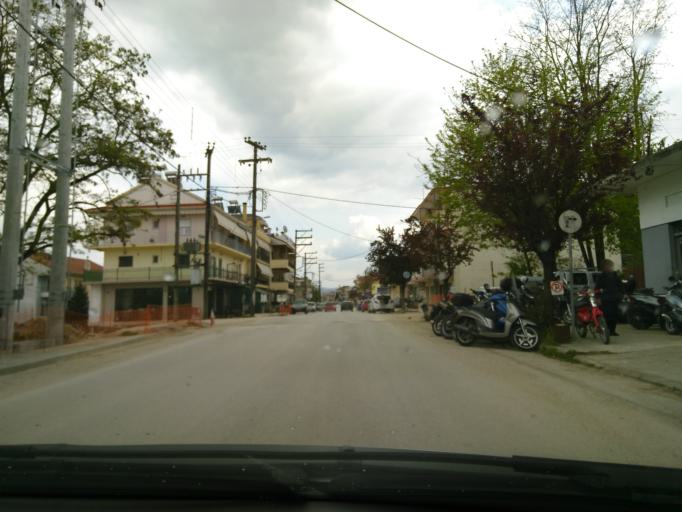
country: GR
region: Epirus
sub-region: Nomos Ioanninon
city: Anatoli
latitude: 39.6440
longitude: 20.8646
